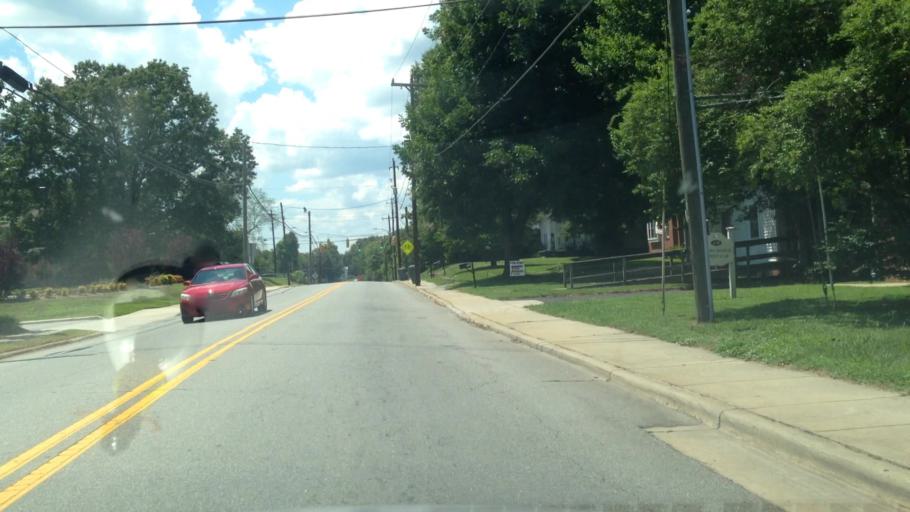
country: US
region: North Carolina
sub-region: Rockingham County
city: Reidsville
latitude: 36.3550
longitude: -79.6671
